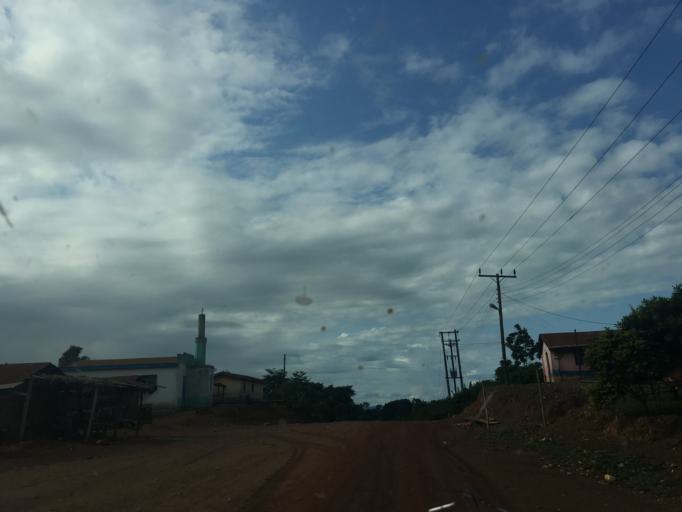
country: GH
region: Western
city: Wassa-Akropong
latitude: 5.9831
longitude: -2.4140
